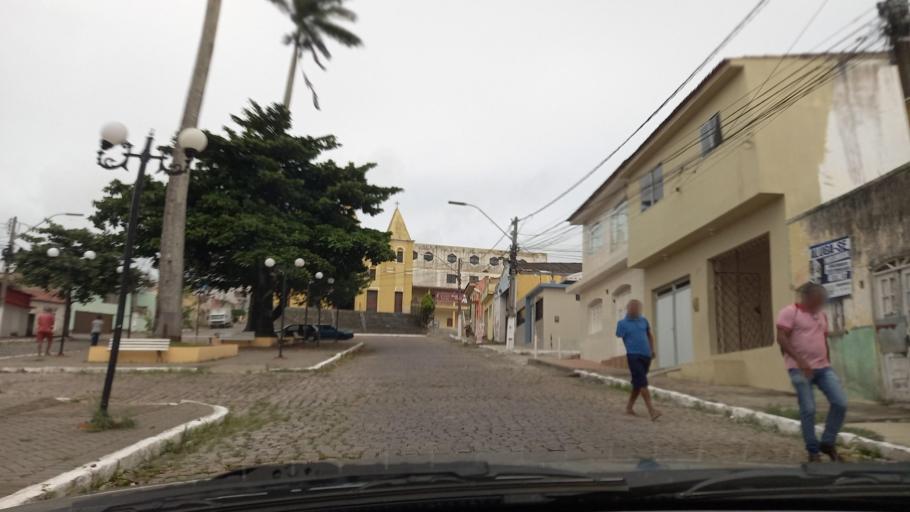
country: BR
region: Pernambuco
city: Garanhuns
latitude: -8.8965
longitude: -36.4950
